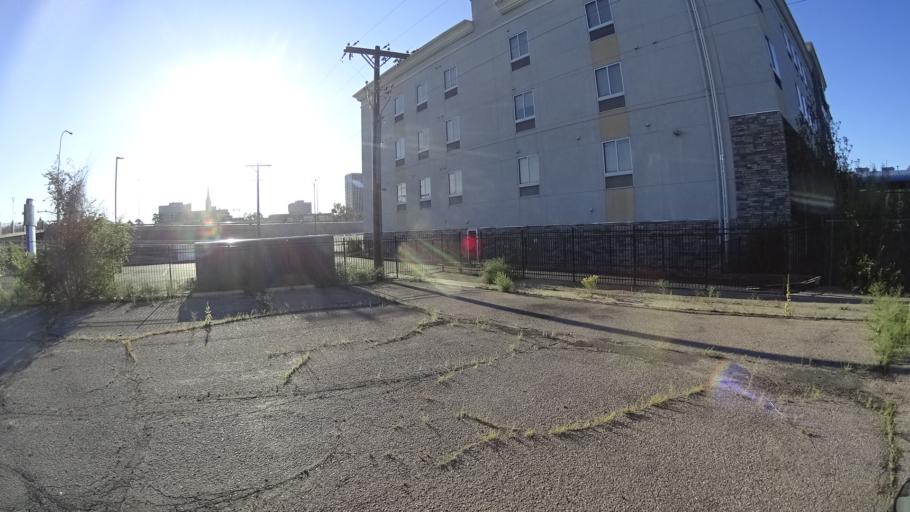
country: US
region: Colorado
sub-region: El Paso County
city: Colorado Springs
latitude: 38.8364
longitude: -104.8315
